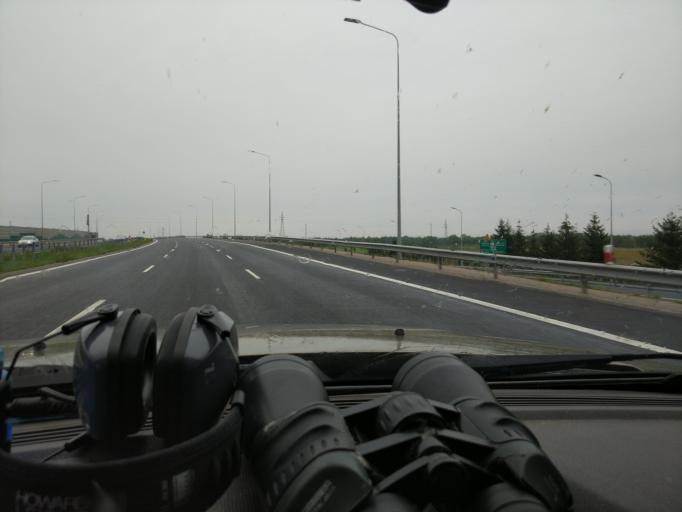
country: PL
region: Masovian Voivodeship
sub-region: Powiat wolominski
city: Radzymin
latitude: 52.3954
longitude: 21.2003
